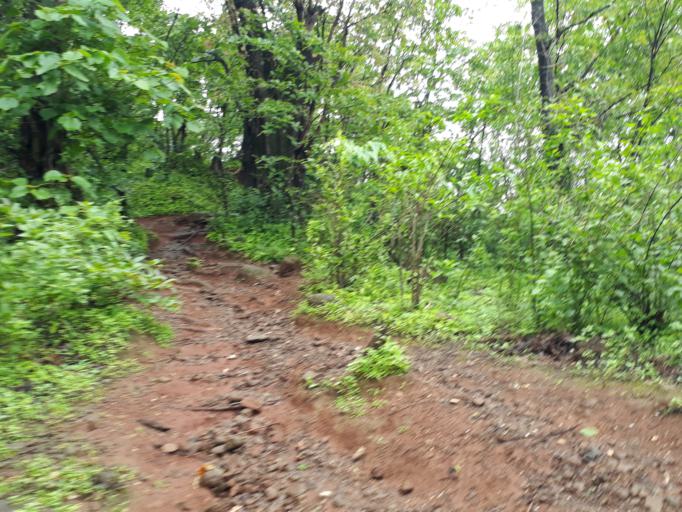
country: IN
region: Maharashtra
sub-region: Raigarh
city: Khopoli
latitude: 18.8411
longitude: 73.3816
